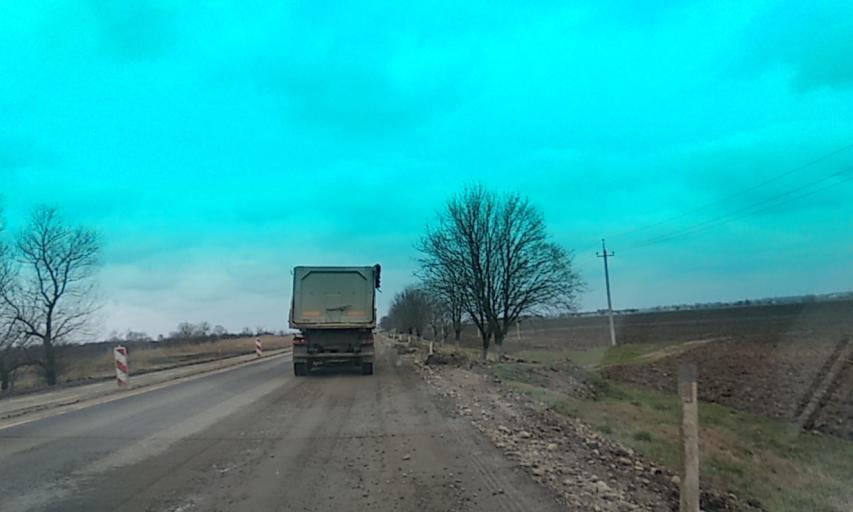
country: RU
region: Krasnodarskiy
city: Velikovechnoye
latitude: 44.9961
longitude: 39.7106
